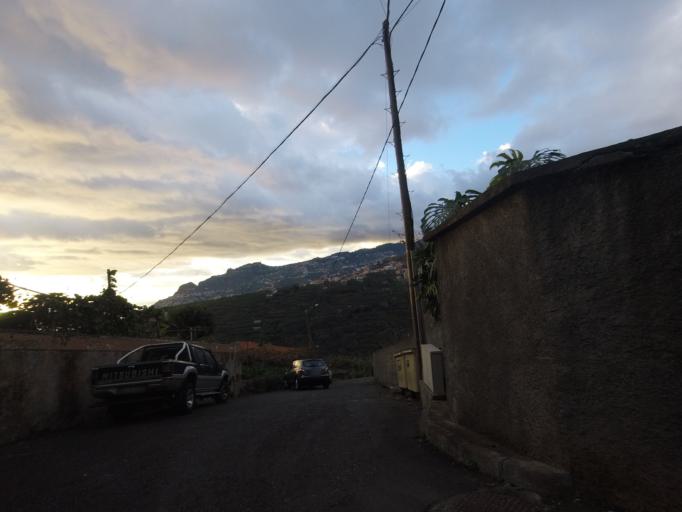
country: PT
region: Madeira
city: Camara de Lobos
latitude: 32.6628
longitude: -16.9555
